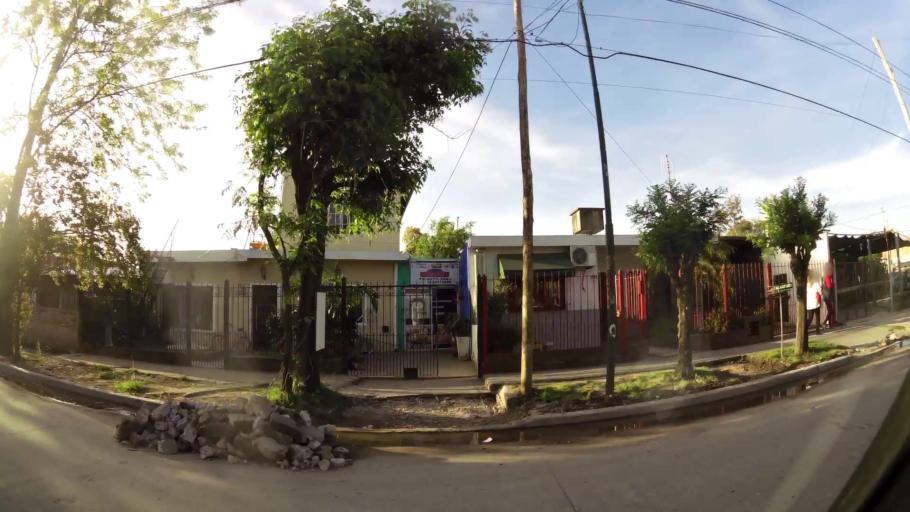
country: AR
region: Buenos Aires
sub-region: Partido de Almirante Brown
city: Adrogue
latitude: -34.7931
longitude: -58.3263
